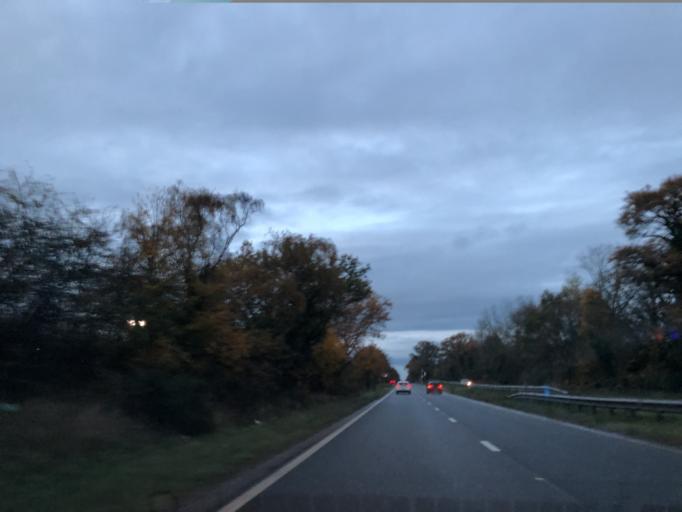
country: GB
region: England
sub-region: Solihull
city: Bickenhill
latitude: 52.4603
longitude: -1.7028
